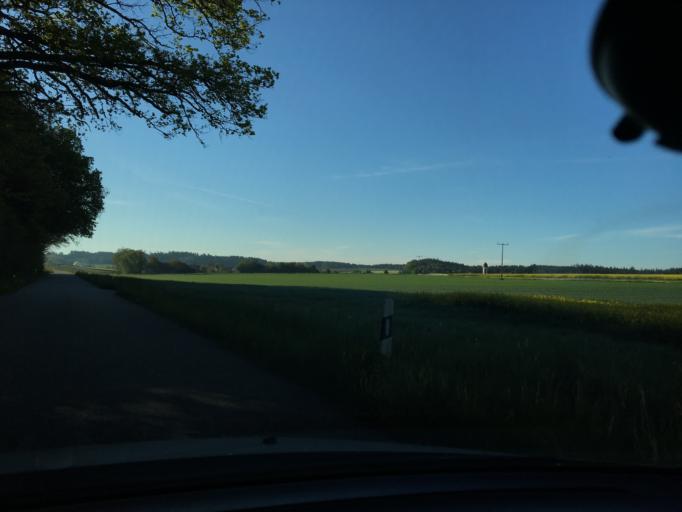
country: DE
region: Bavaria
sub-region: Lower Bavaria
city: Vilsbiburg
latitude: 48.5036
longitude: 12.3400
